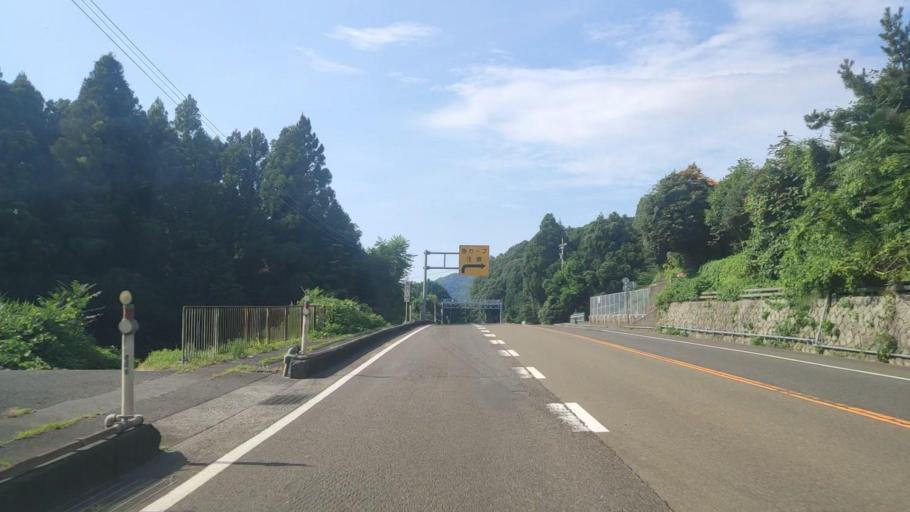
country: JP
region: Fukui
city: Tsuruga
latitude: 35.7497
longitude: 136.1043
